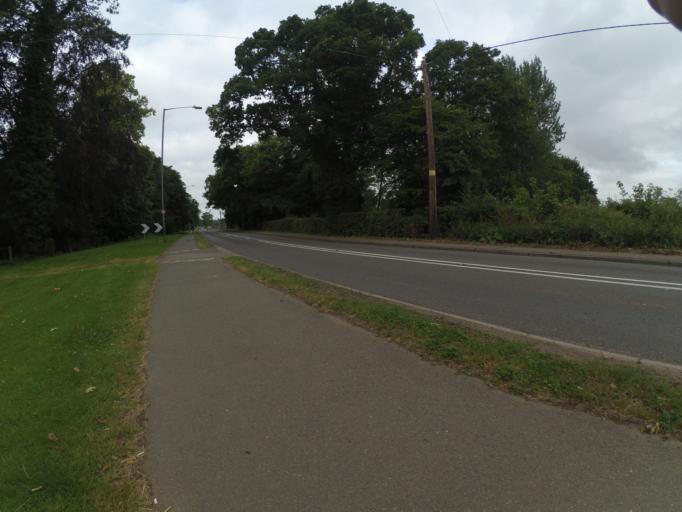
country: GB
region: England
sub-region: Warwickshire
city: Rugby
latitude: 52.3493
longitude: -1.2566
